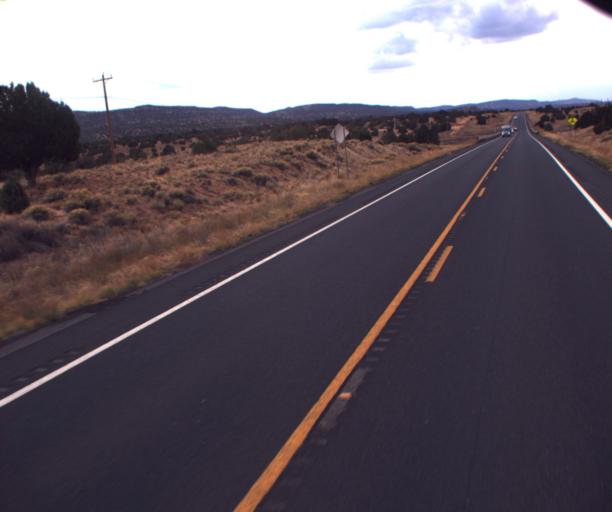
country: US
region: Arizona
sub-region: Navajo County
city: Kayenta
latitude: 36.4966
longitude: -110.6237
